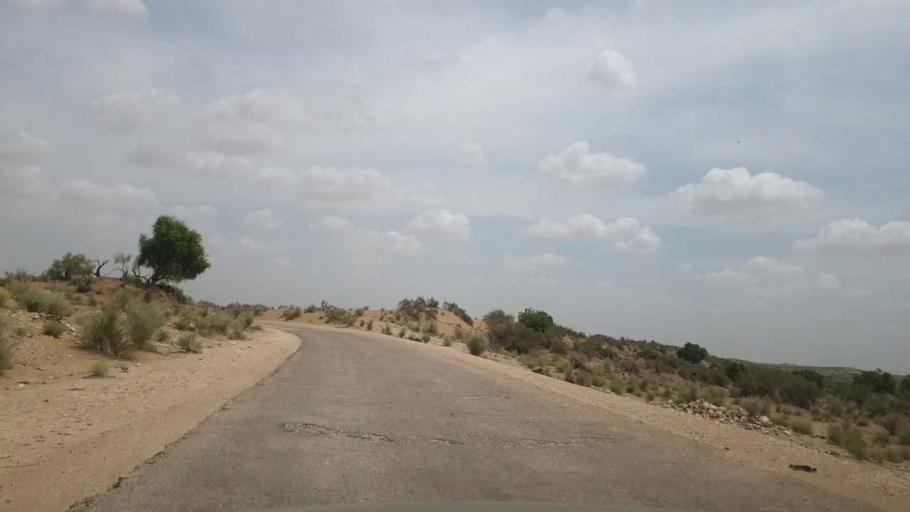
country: PK
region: Sindh
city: Kot Diji
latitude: 27.1570
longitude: 69.2234
